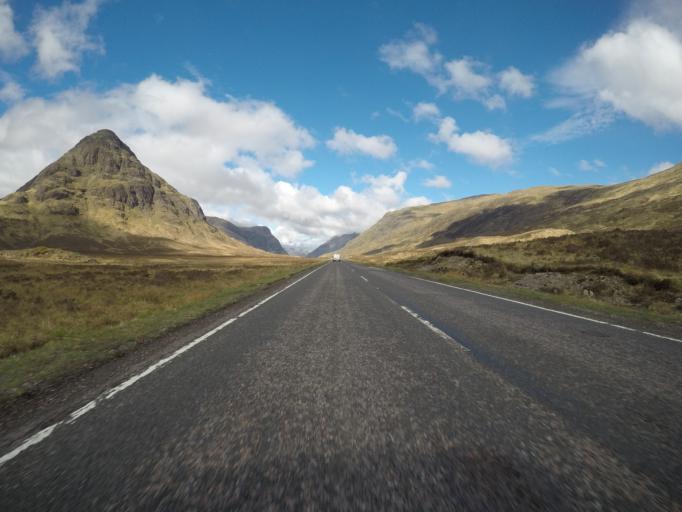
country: GB
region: Scotland
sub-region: Highland
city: Spean Bridge
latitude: 56.6619
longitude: -4.9212
